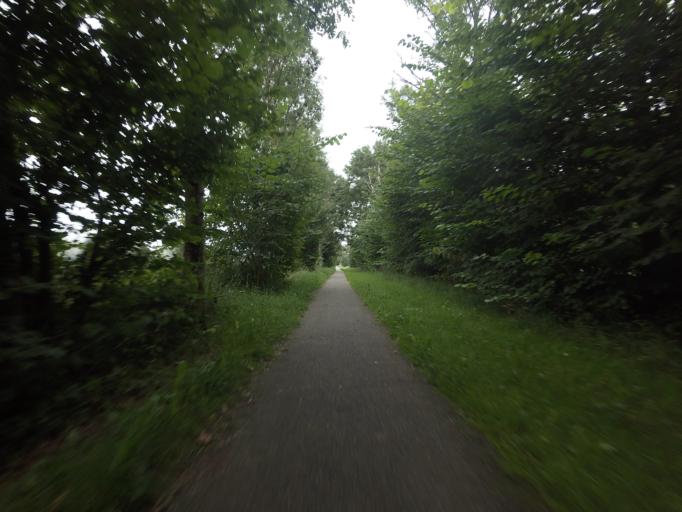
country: DK
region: Central Jutland
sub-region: Horsens Kommune
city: Braedstrup
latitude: 56.0224
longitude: 9.5707
